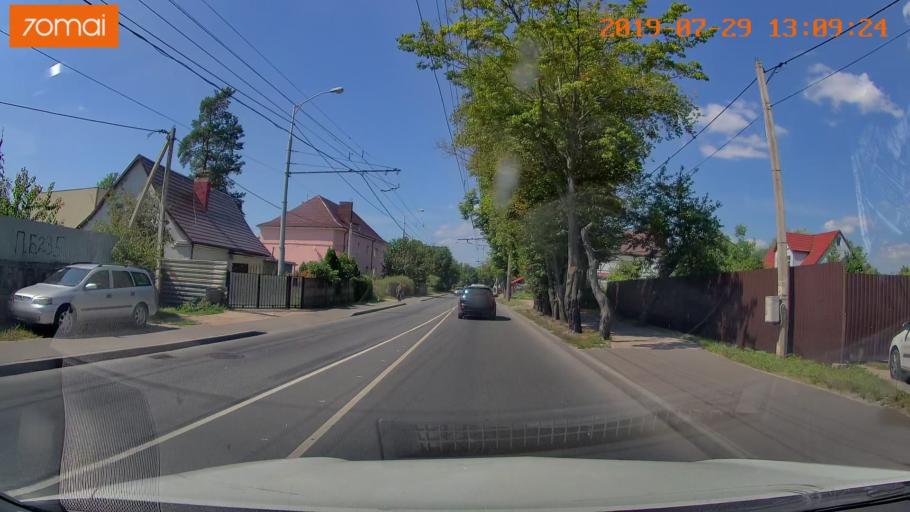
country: RU
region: Kaliningrad
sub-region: Gorod Kaliningrad
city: Kaliningrad
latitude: 54.7137
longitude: 20.4181
